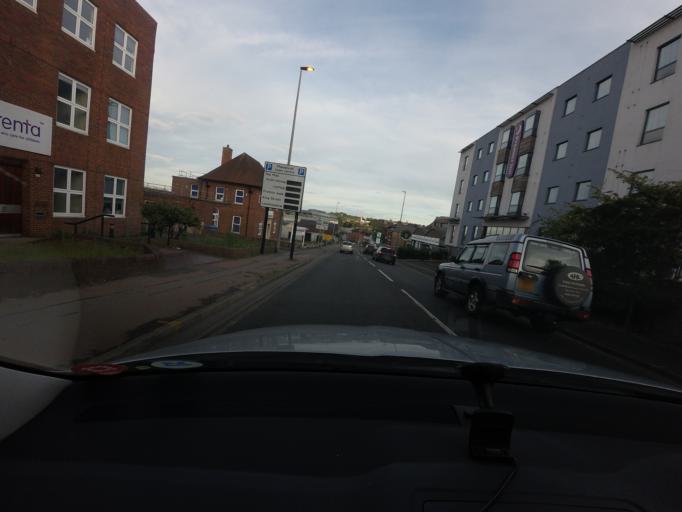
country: GB
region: England
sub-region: Kent
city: Maidstone
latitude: 51.2720
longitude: 0.5138
